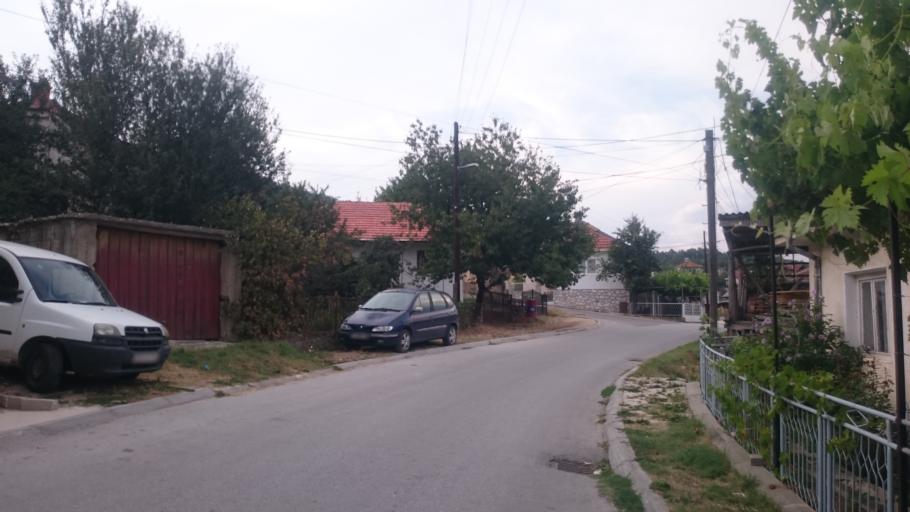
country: MK
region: Makedonski Brod
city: Makedonski Brod
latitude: 41.5153
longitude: 21.2130
